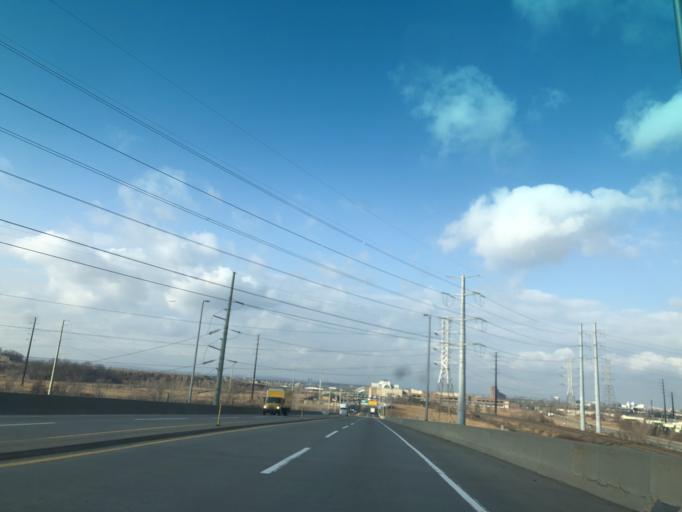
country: US
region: New Jersey
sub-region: Hudson County
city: Jersey City
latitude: 40.7516
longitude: -74.0707
